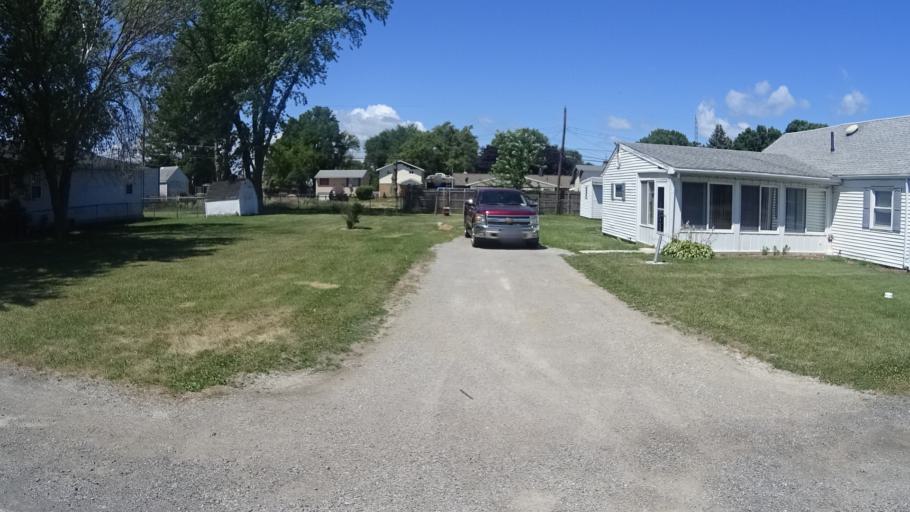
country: US
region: Ohio
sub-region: Erie County
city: Sandusky
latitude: 41.4344
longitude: -82.7343
